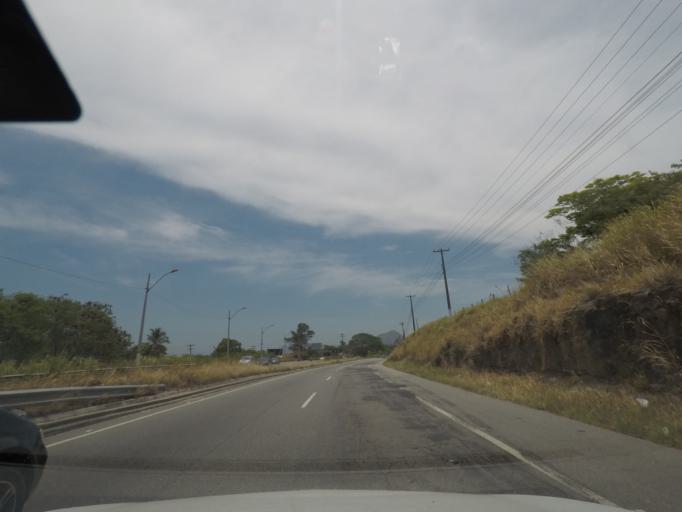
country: BR
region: Rio de Janeiro
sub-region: Marica
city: Marica
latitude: -22.9356
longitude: -42.9040
